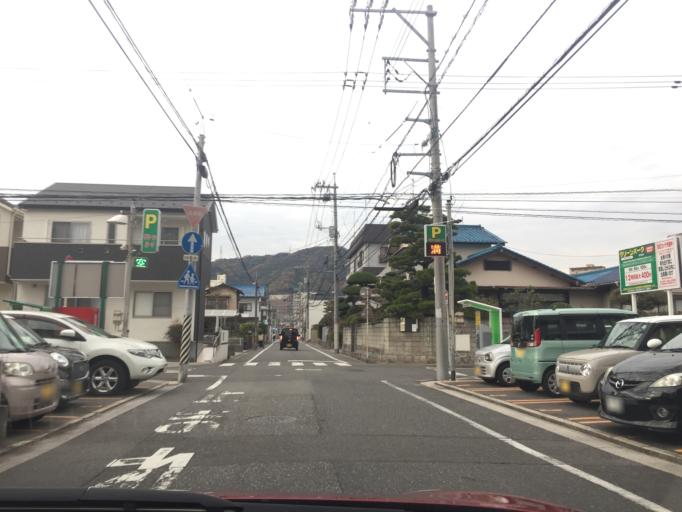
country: JP
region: Hiroshima
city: Hiroshima-shi
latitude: 34.3866
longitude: 132.4212
